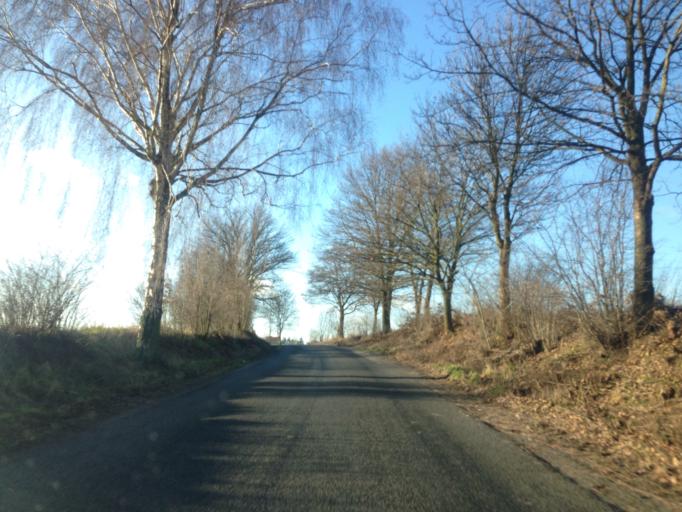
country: PL
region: Kujawsko-Pomorskie
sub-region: Powiat grudziadzki
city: Swiecie nad Osa
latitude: 53.4152
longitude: 19.1224
